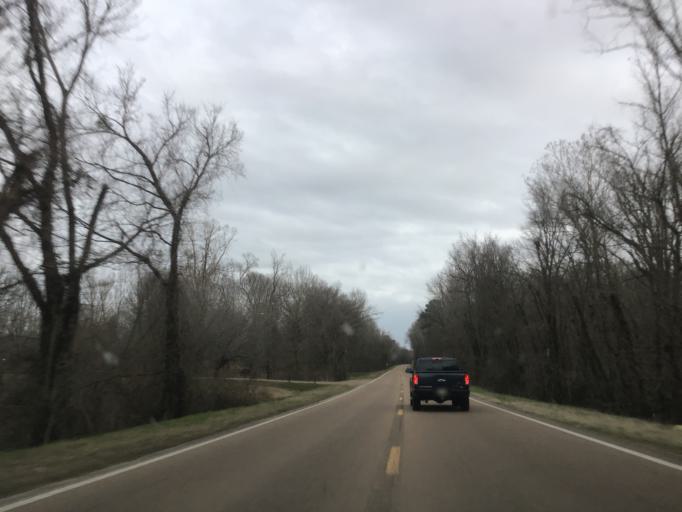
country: US
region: Mississippi
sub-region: Warren County
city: Beechwood
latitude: 32.3103
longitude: -90.8068
